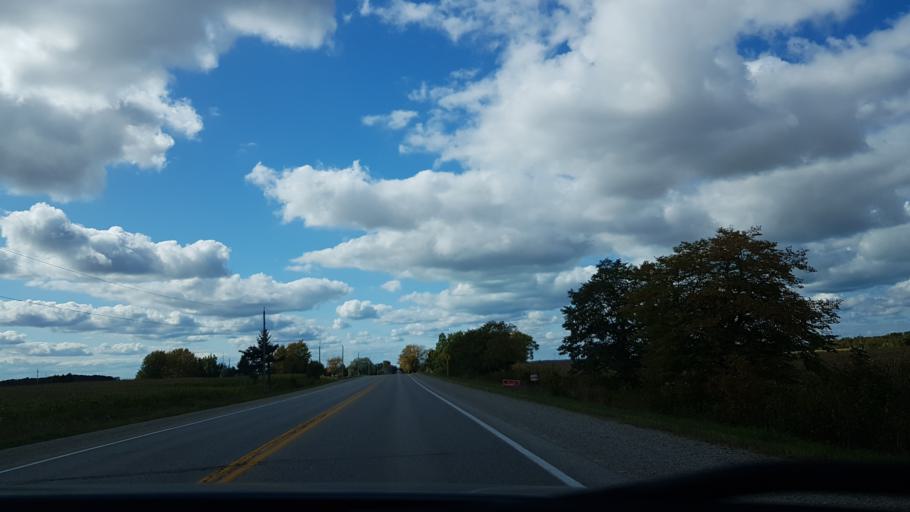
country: CA
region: Ontario
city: South Huron
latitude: 43.3490
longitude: -81.6059
